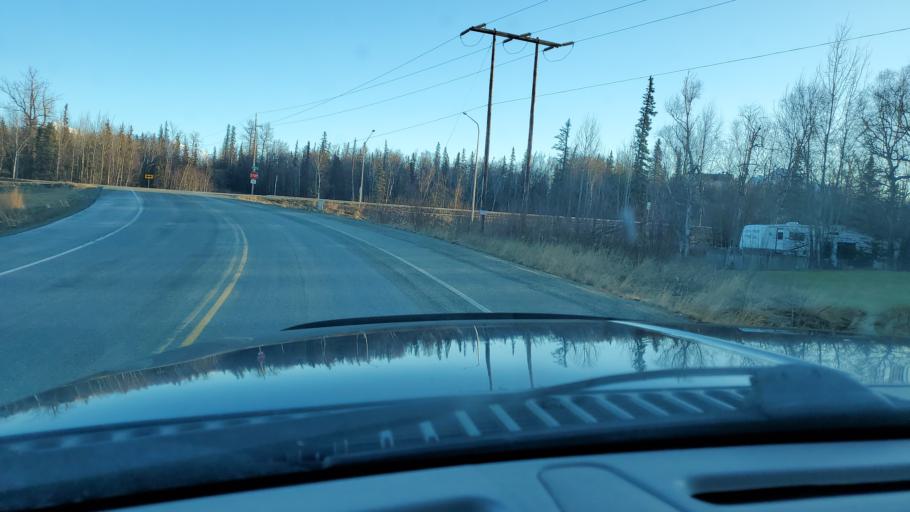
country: US
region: Alaska
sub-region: Matanuska-Susitna Borough
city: Gateway
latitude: 61.5925
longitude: -149.2402
